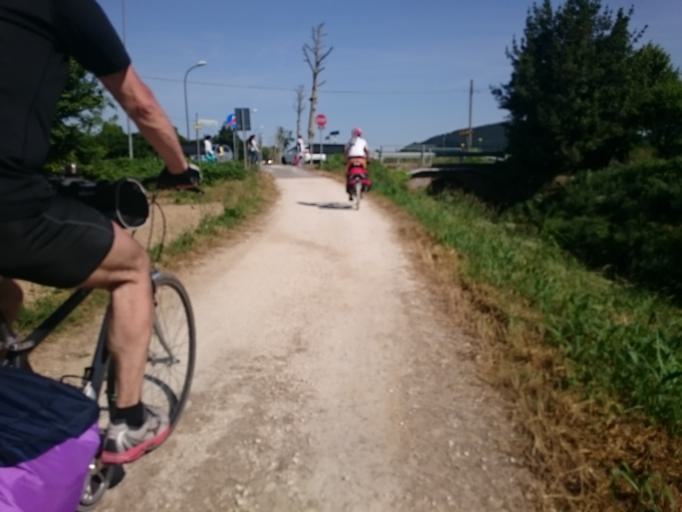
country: IT
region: Veneto
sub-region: Provincia di Padova
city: San Biagio
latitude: 45.3692
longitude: 11.7356
